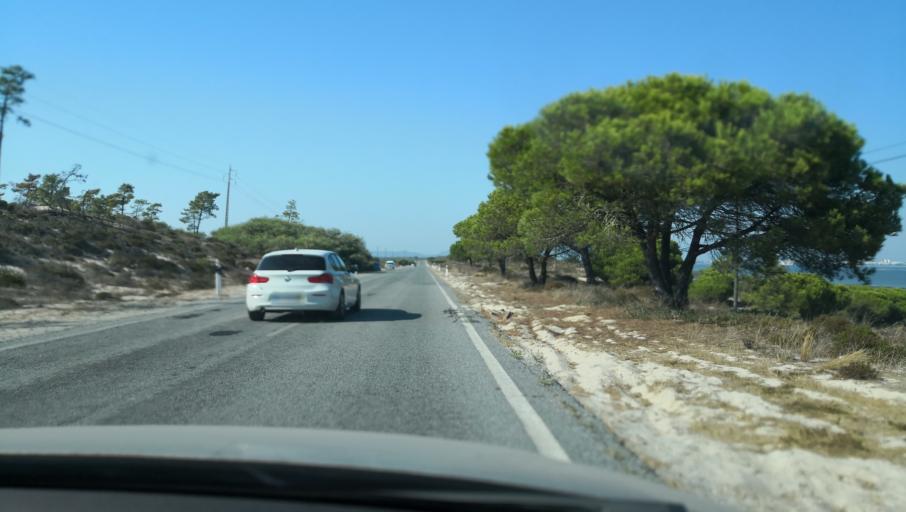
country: PT
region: Setubal
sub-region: Setubal
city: Setubal
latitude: 38.4222
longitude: -8.8217
